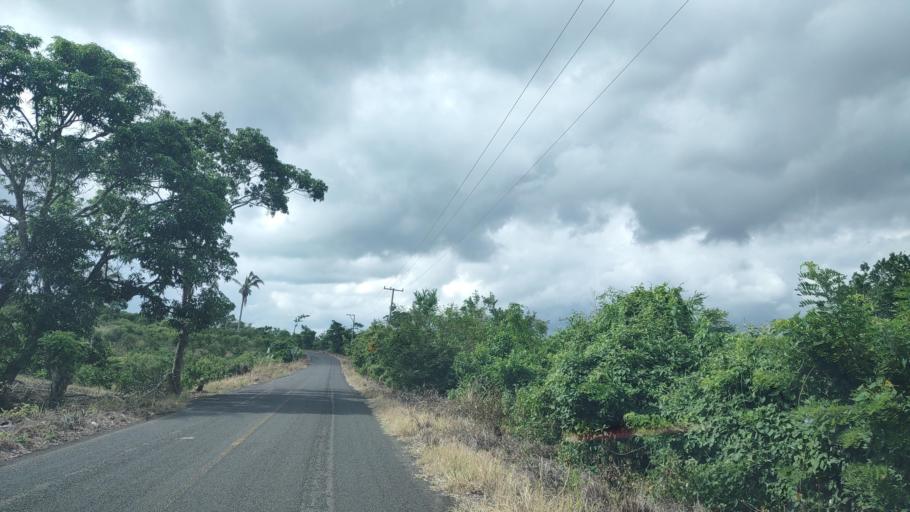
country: MX
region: Veracruz
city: Gutierrez Zamora
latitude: 20.2967
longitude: -97.1355
